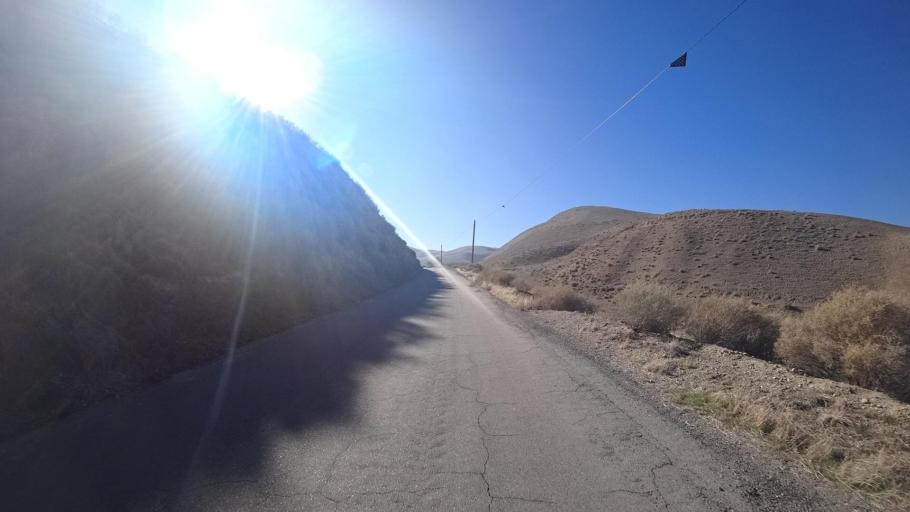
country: US
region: California
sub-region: Kern County
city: Maricopa
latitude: 34.9822
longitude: -119.3996
